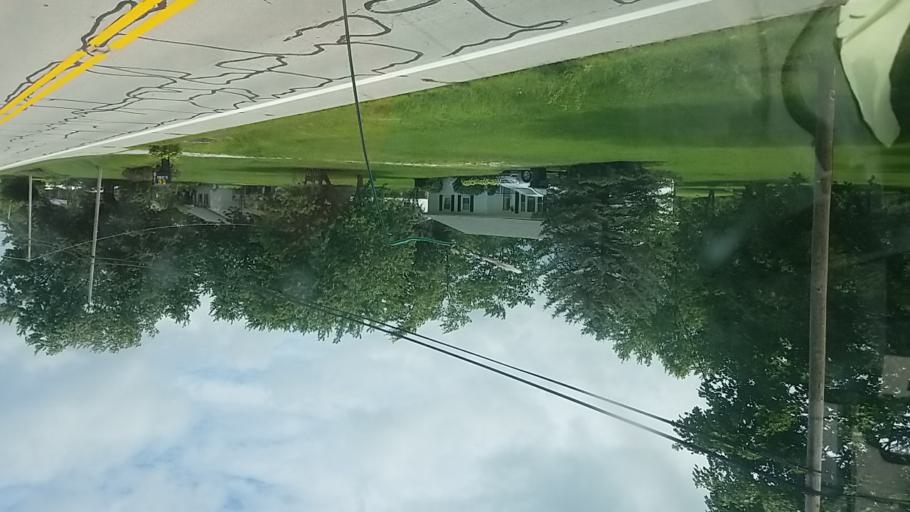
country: US
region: Ohio
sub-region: Fayette County
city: Jeffersonville
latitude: 39.6586
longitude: -83.5683
